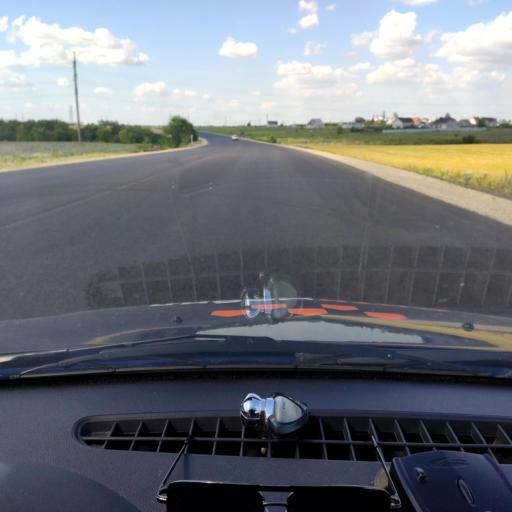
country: RU
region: Voronezj
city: Novovoronezh
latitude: 51.3523
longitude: 39.2778
